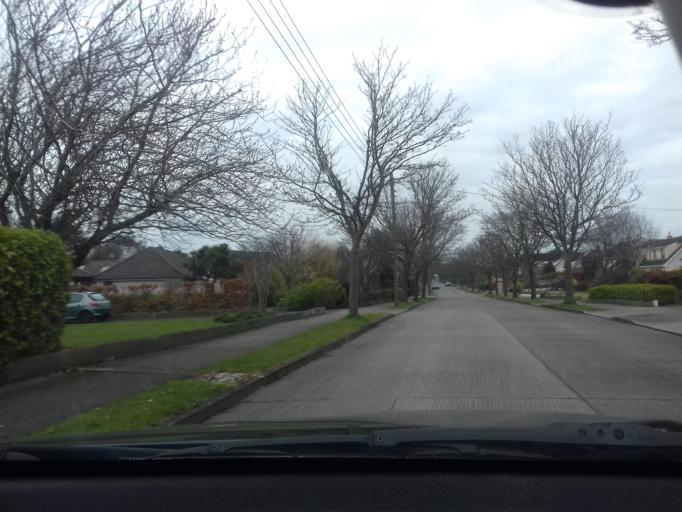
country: IE
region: Leinster
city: Sutton
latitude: 53.3871
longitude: -6.0983
